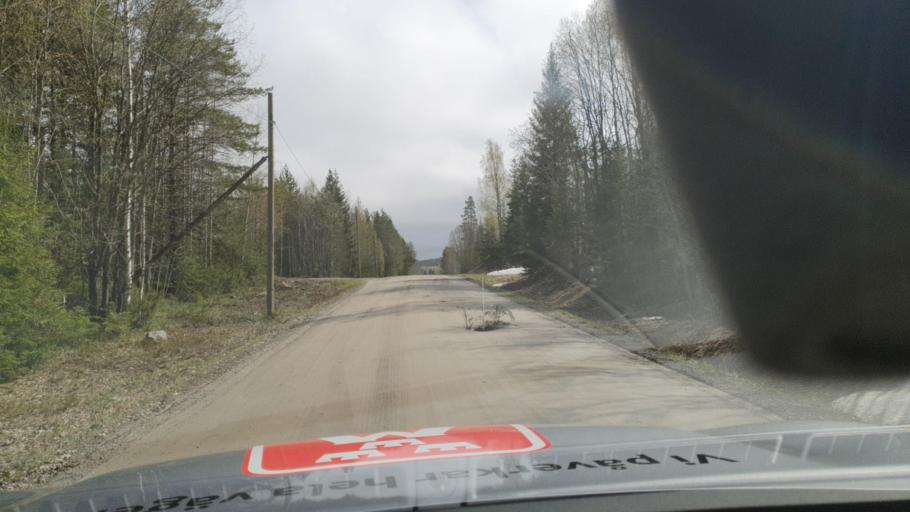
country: SE
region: Vaesterbotten
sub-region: Bjurholms Kommun
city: Bjurholm
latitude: 63.6761
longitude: 18.9927
